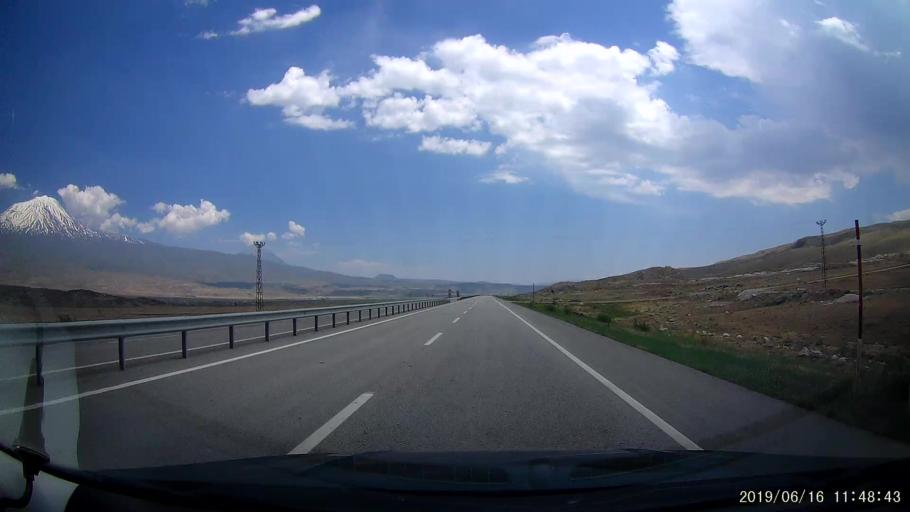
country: TR
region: Agri
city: Dogubayazit
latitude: 39.5579
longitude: 44.1491
